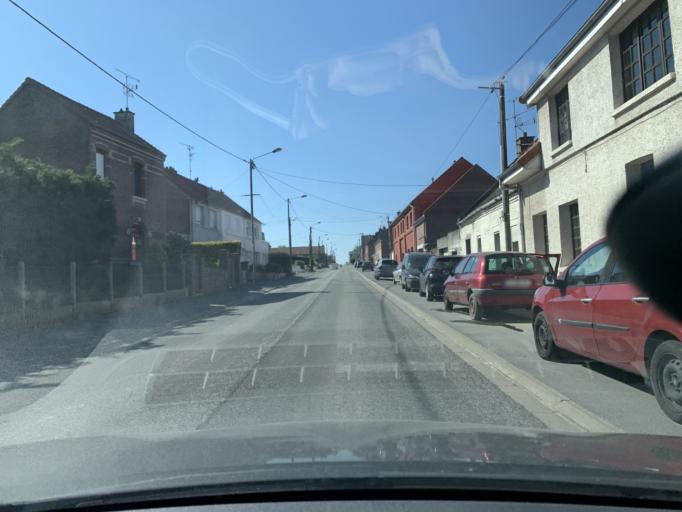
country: FR
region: Nord-Pas-de-Calais
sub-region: Departement du Nord
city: Cambrai
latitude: 50.1578
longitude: 3.2418
